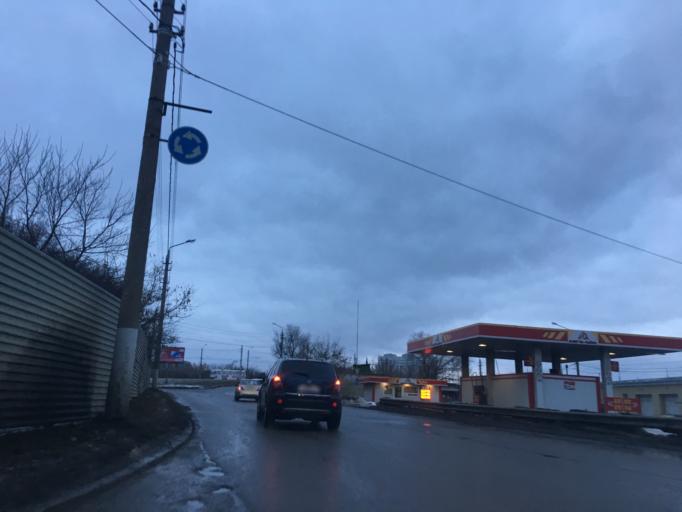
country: RU
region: Tula
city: Tula
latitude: 54.2034
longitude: 37.5887
